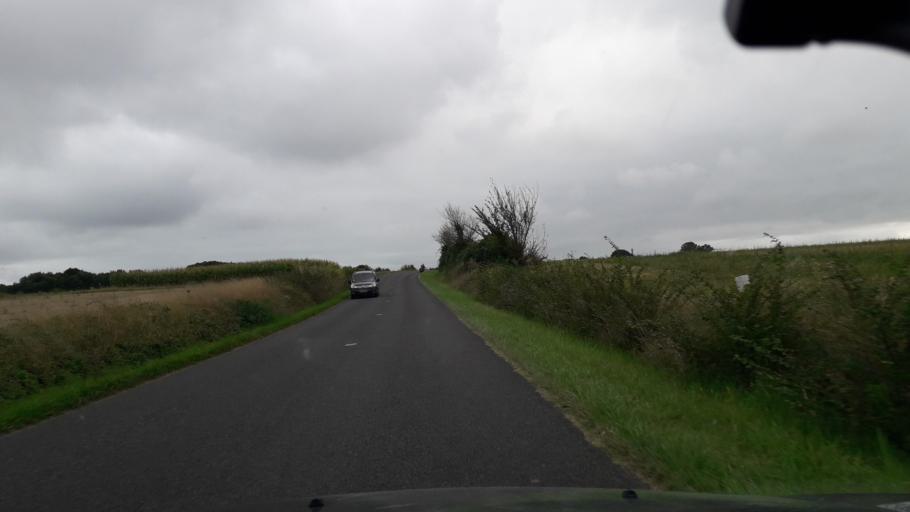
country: FR
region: Poitou-Charentes
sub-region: Departement de la Charente-Maritime
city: Arvert
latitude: 45.7285
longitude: -1.1367
